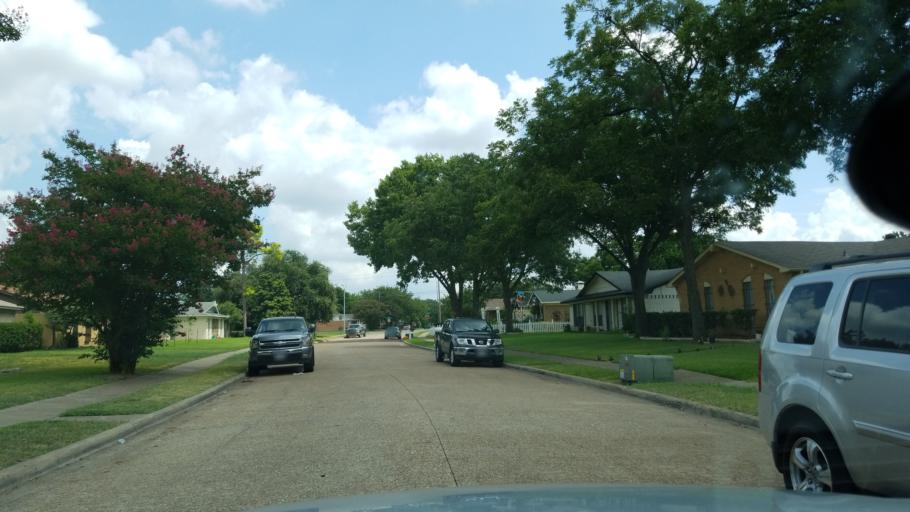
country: US
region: Texas
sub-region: Dallas County
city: Garland
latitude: 32.9262
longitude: -96.6497
